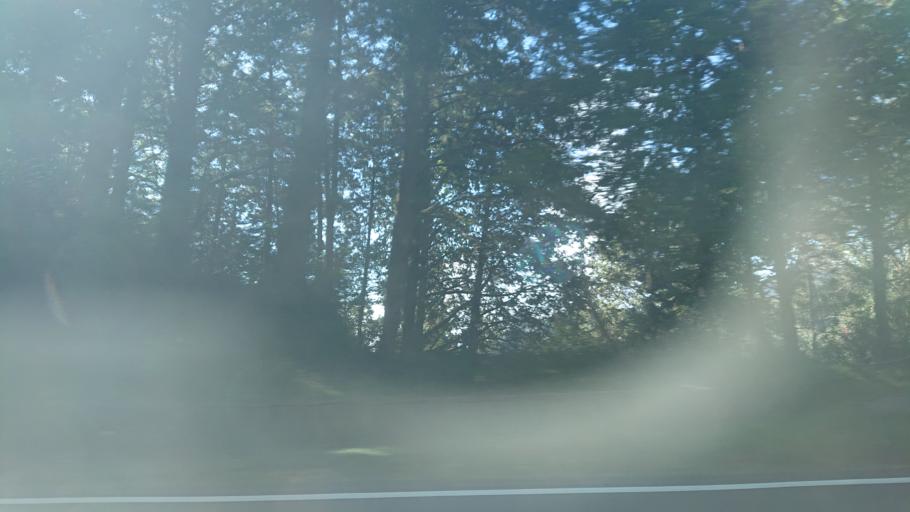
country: TW
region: Taiwan
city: Lugu
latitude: 23.4910
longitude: 120.8191
